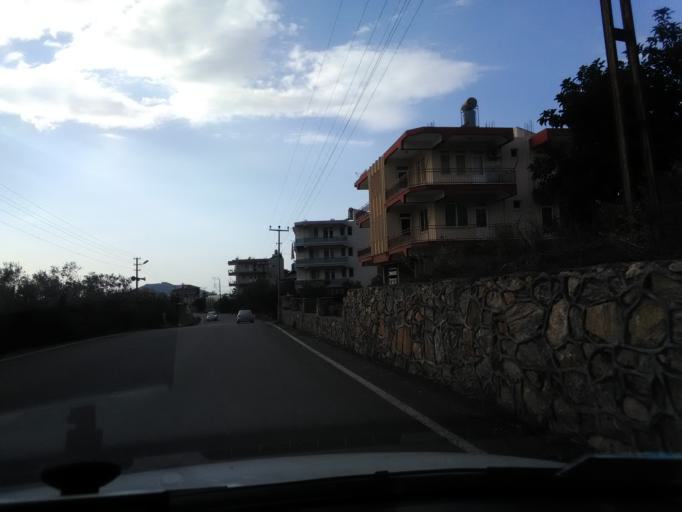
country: TR
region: Antalya
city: Gazipasa
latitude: 36.2740
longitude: 32.3409
